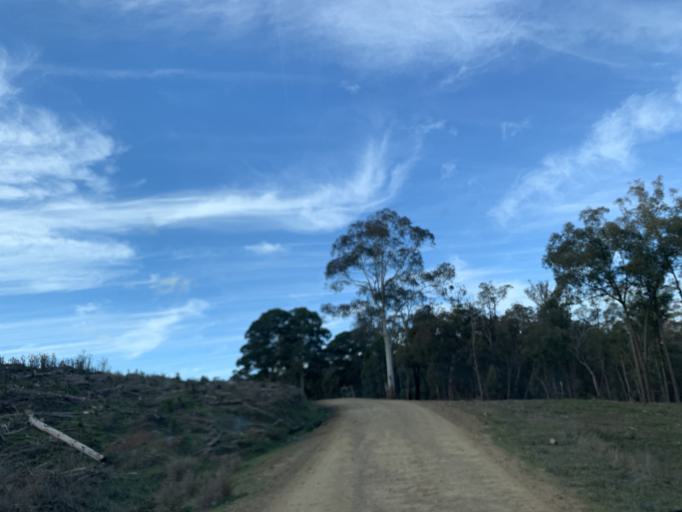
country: AU
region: Victoria
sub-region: Mansfield
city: Mansfield
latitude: -36.9286
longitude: 146.0942
